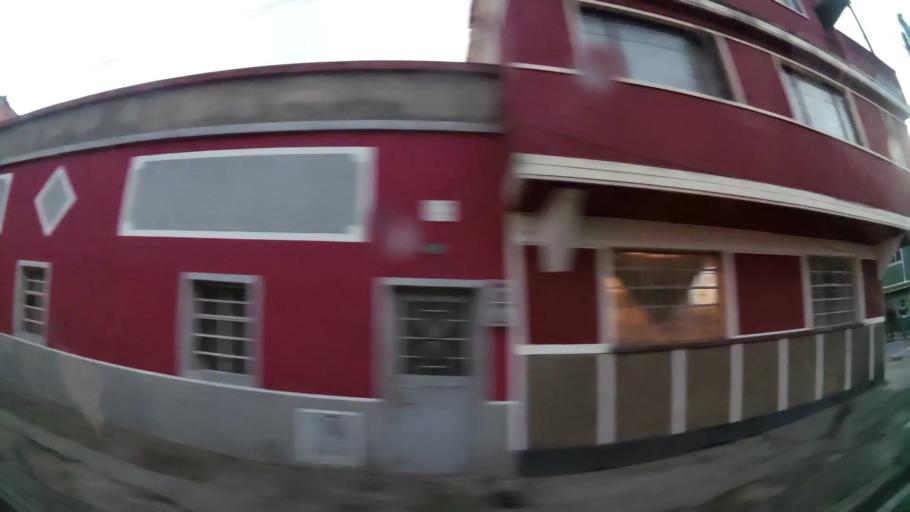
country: CO
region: Bogota D.C.
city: Barrio San Luis
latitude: 4.6765
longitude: -74.0768
